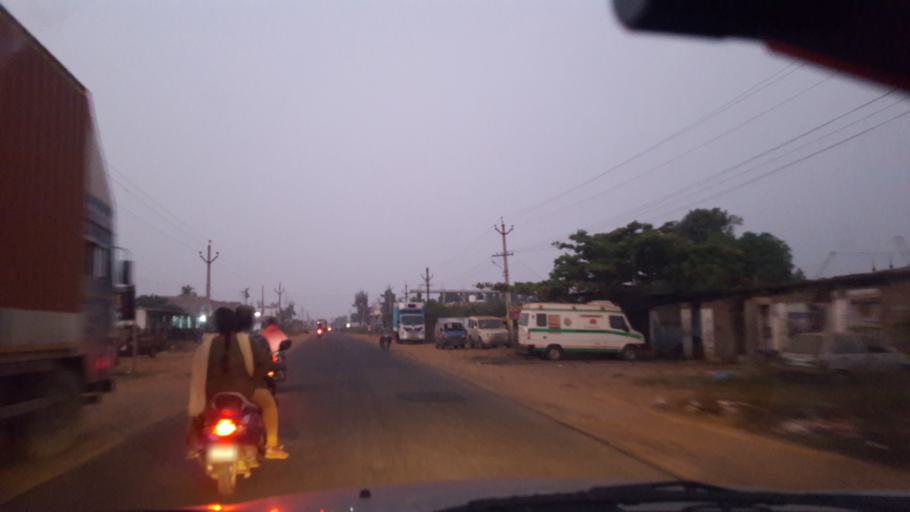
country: IN
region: Andhra Pradesh
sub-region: Srikakulam
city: Palasa
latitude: 18.7462
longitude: 84.4152
